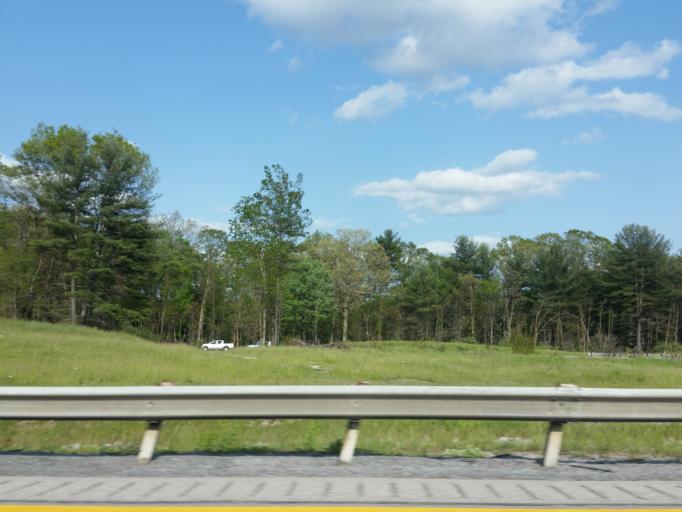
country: US
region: West Virginia
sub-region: Mercer County
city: Athens
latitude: 37.4286
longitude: -81.0671
